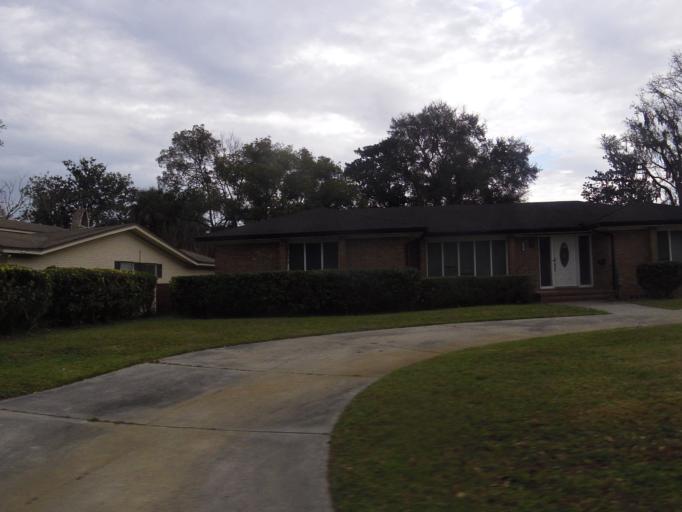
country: US
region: Florida
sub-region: Duval County
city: Jacksonville
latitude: 30.3314
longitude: -81.6105
